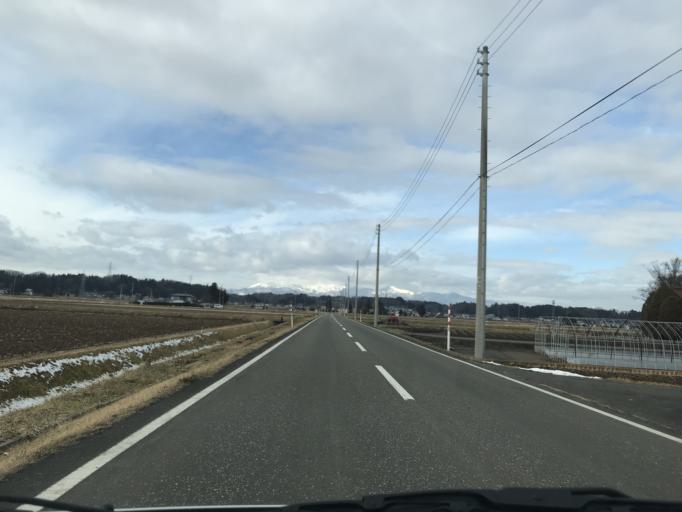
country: JP
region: Iwate
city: Mizusawa
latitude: 39.0897
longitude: 141.1499
